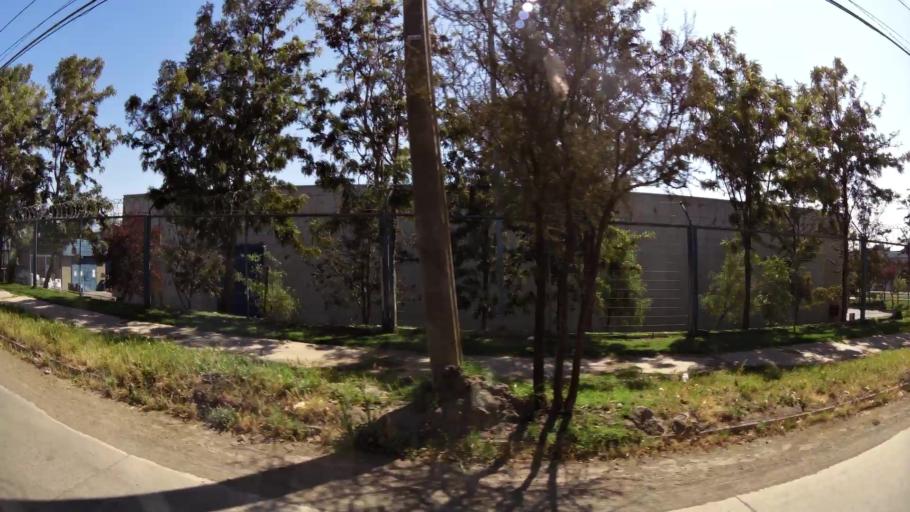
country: CL
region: Santiago Metropolitan
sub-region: Provincia de Santiago
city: Lo Prado
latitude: -33.3835
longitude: -70.7433
